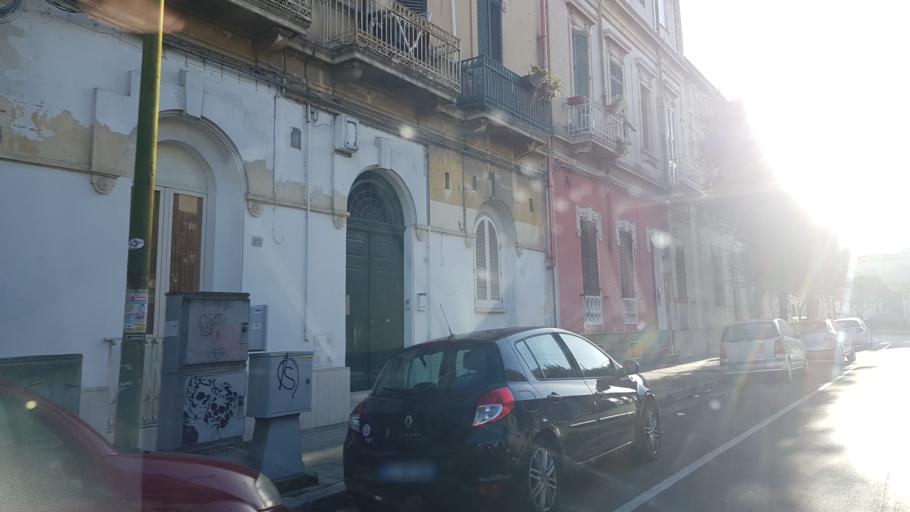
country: IT
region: Apulia
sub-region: Provincia di Lecce
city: Lecce
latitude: 40.3502
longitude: 18.1625
